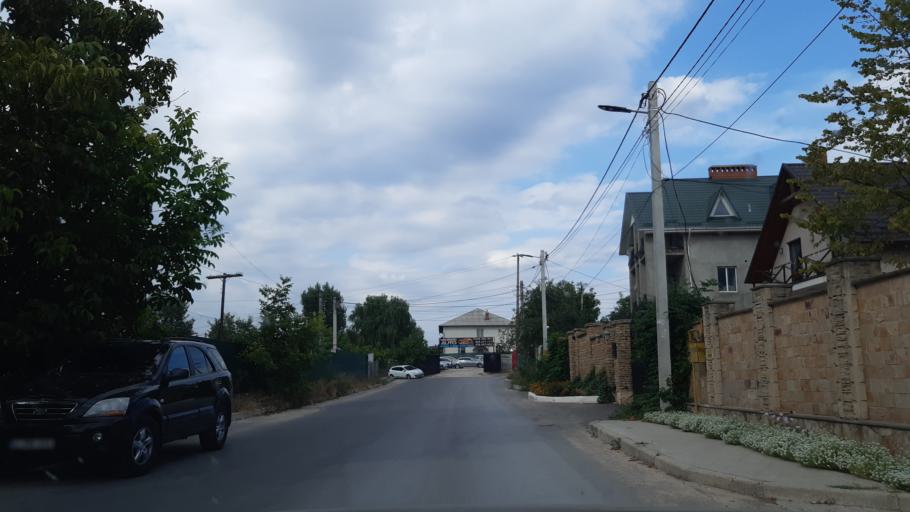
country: MD
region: Chisinau
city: Vatra
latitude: 47.0483
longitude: 28.7381
